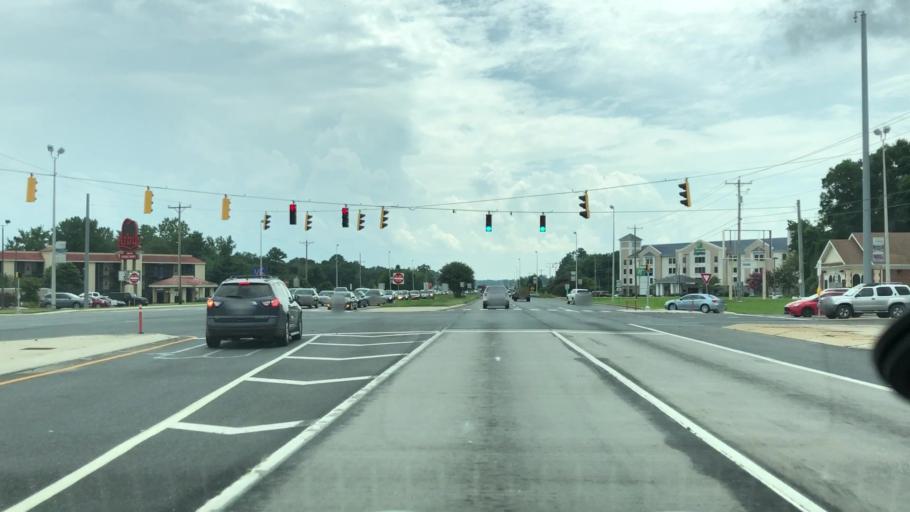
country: US
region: Delaware
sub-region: Sussex County
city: Seaford
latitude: 38.6531
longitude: -75.5945
